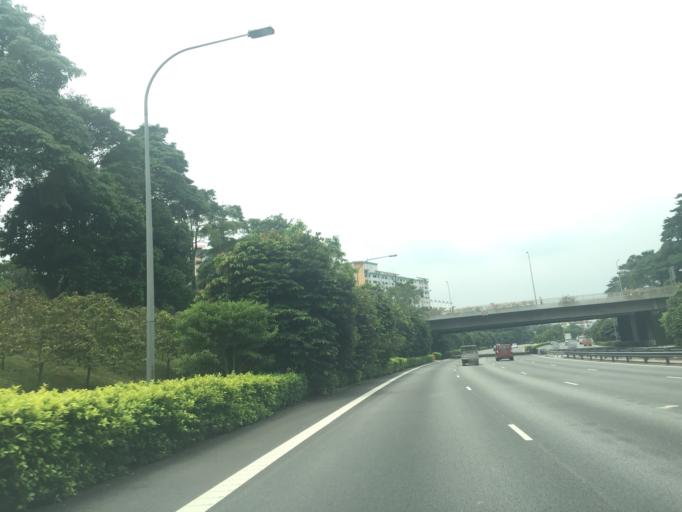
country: MY
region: Johor
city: Johor Bahru
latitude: 1.3890
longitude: 103.7444
